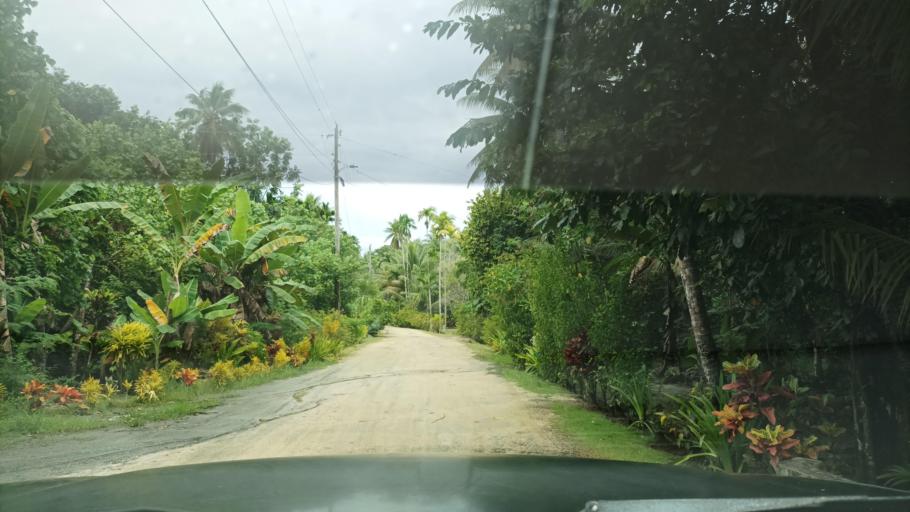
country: FM
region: Yap
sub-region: Rumung Municipality
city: Rumung
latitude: 9.5524
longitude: 138.1931
